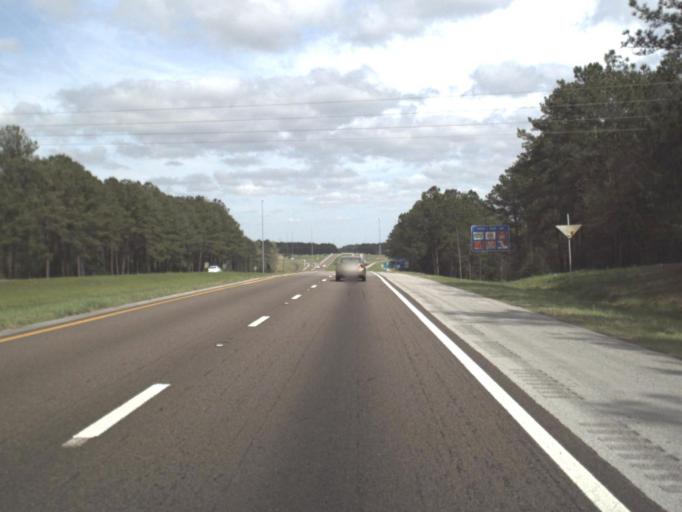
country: US
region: Florida
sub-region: Walton County
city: DeFuniak Springs
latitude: 30.6930
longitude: -86.1360
